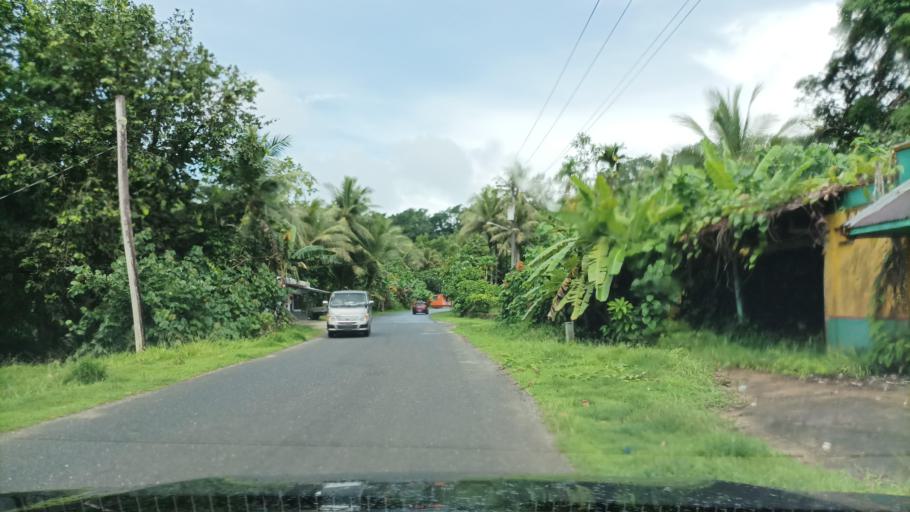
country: FM
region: Pohnpei
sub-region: Madolenihm Municipality
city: Madolenihm Municipality Government
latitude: 6.9141
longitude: 158.3015
